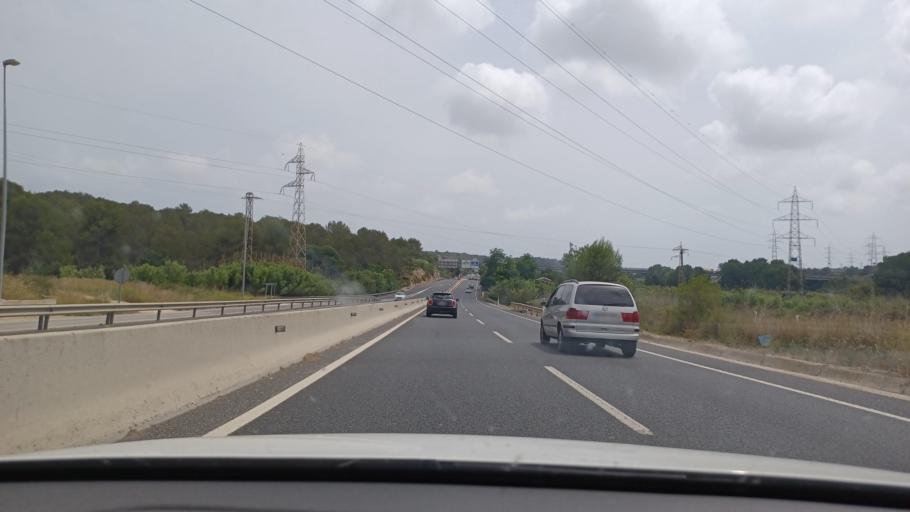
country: ES
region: Catalonia
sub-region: Provincia de Tarragona
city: Constanti
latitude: 41.1505
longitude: 1.2397
